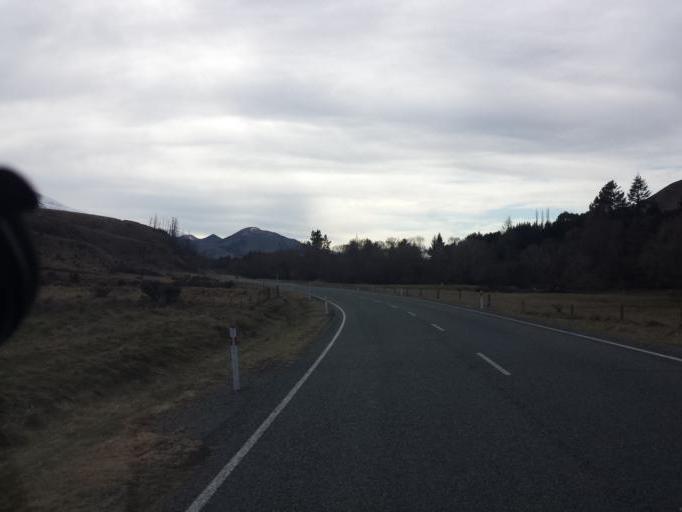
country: NZ
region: Canterbury
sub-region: Timaru District
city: Pleasant Point
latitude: -44.0638
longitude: 170.6731
